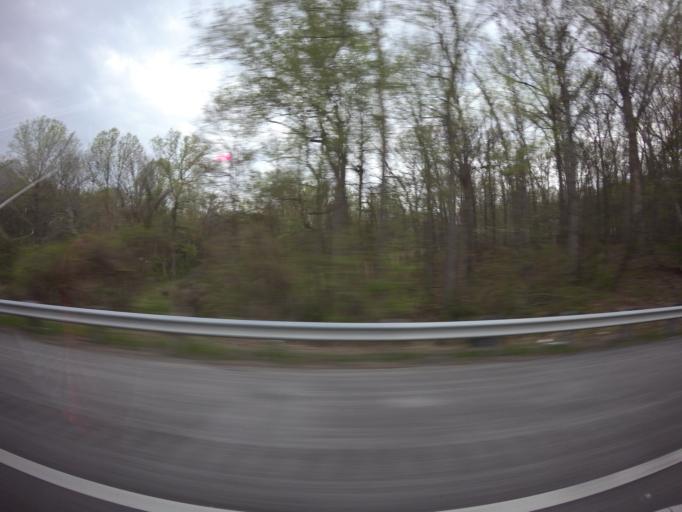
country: US
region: Maryland
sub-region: Howard County
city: Columbia
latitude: 39.3051
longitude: -76.8957
